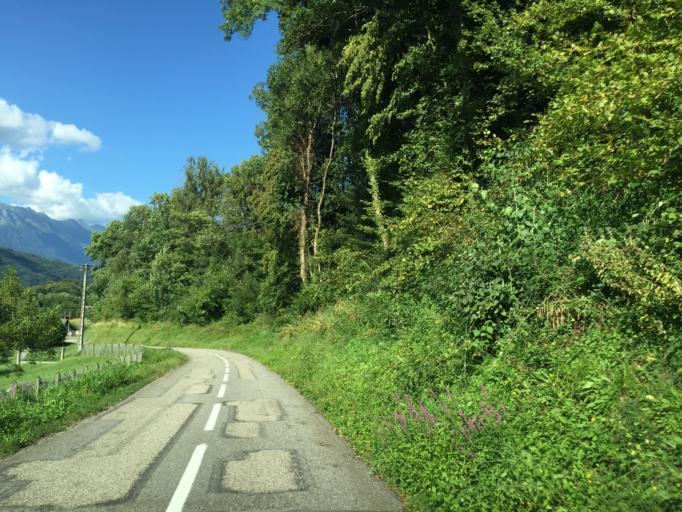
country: FR
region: Rhone-Alpes
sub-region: Departement de la Savoie
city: La Rochette
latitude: 45.4855
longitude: 6.1529
